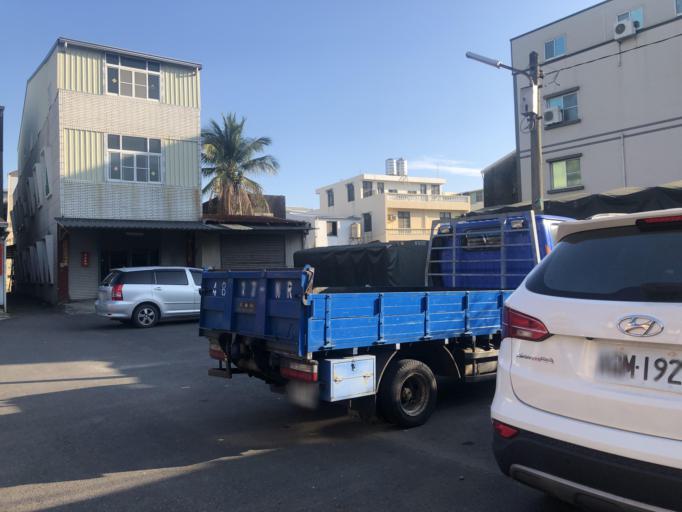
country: TW
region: Taiwan
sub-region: Tainan
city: Tainan
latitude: 23.0411
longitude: 120.1829
